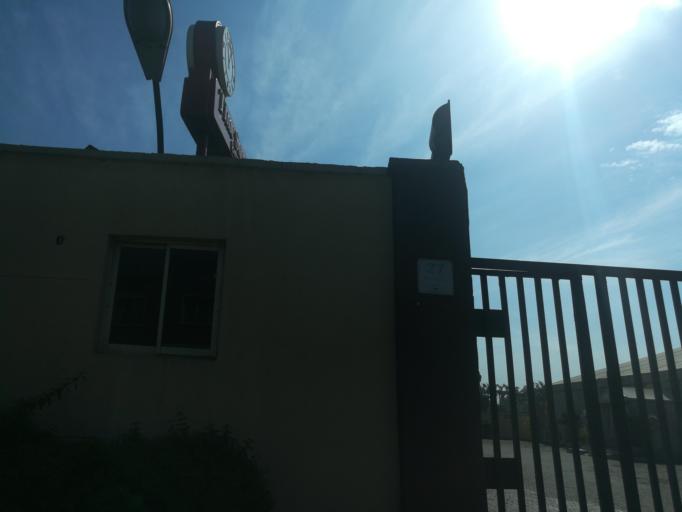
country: NG
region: Lagos
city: Ikeja
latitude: 6.6021
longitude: 3.3405
